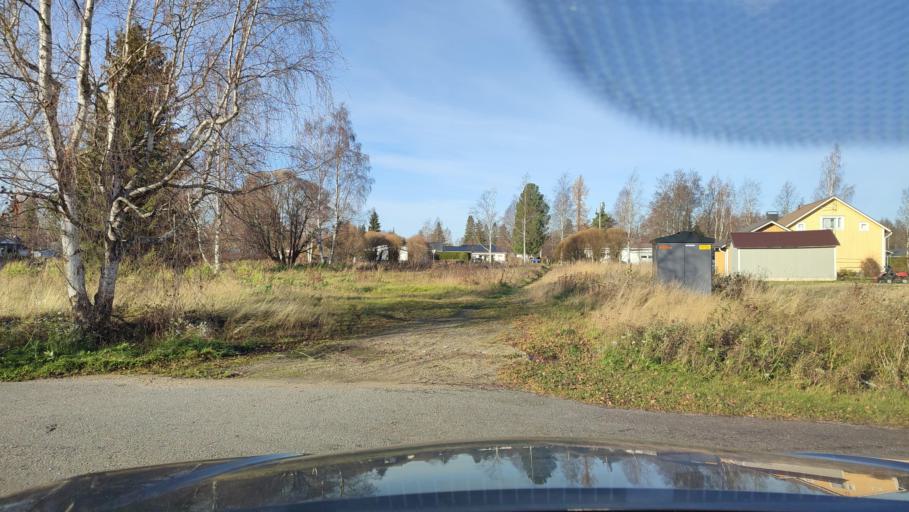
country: FI
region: Southern Ostrobothnia
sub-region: Suupohja
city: Teuva
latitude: 62.4786
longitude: 21.7513
